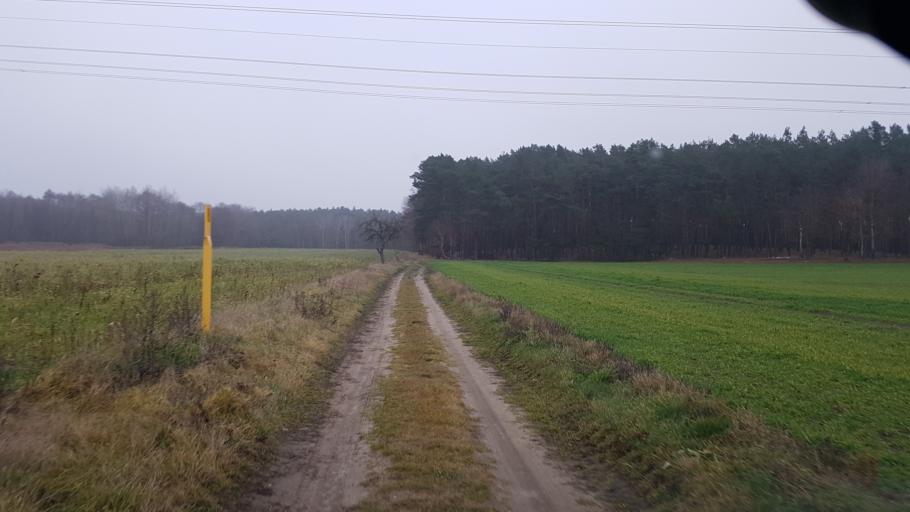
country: DE
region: Brandenburg
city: Altdobern
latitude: 51.6779
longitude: 13.9970
